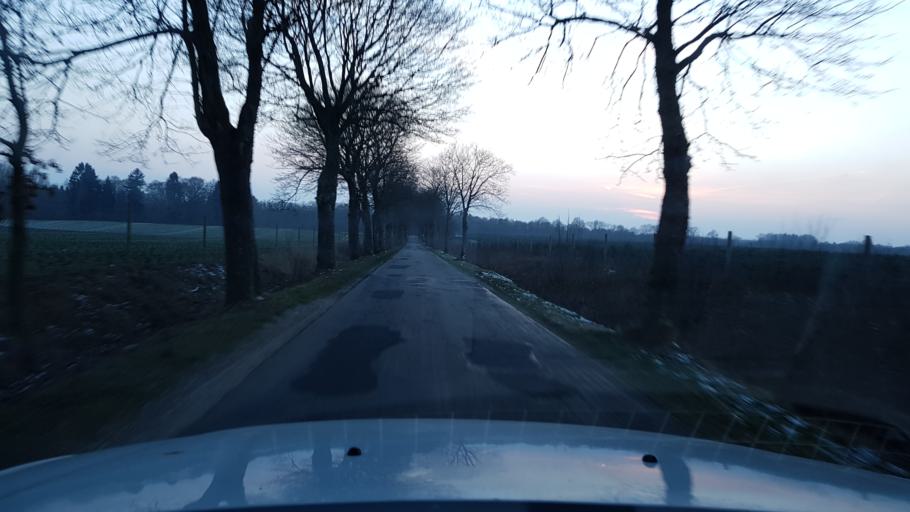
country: PL
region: West Pomeranian Voivodeship
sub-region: Powiat bialogardzki
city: Karlino
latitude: 54.0135
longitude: 15.8436
